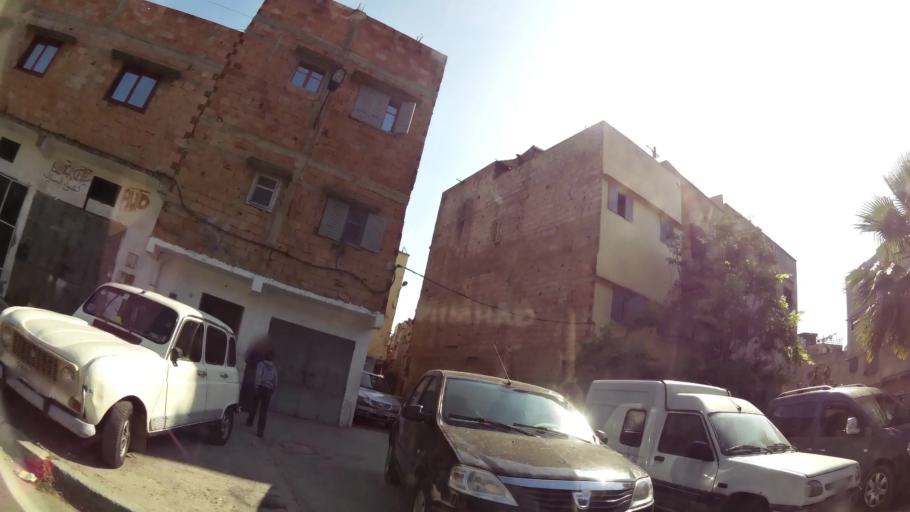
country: MA
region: Rabat-Sale-Zemmour-Zaer
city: Sale
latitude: 34.0579
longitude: -6.7723
